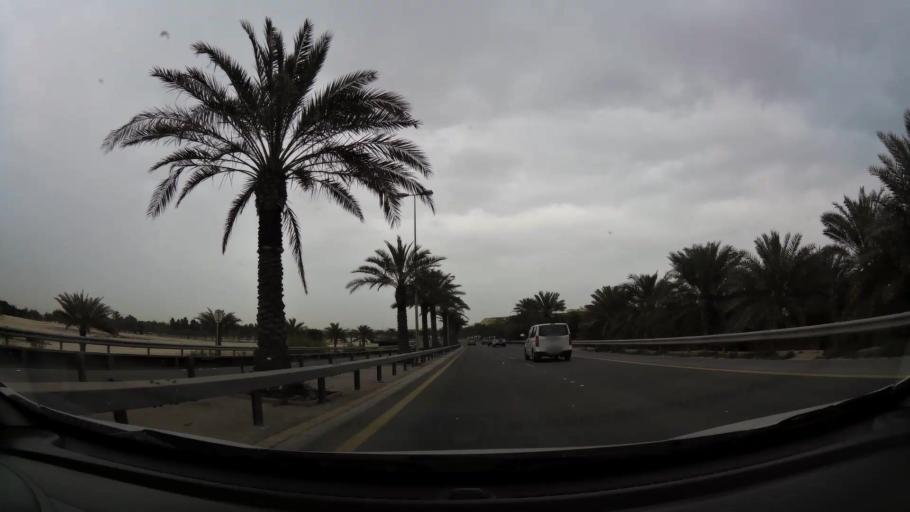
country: BH
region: Northern
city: Ar Rifa'
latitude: 26.1146
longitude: 50.5373
